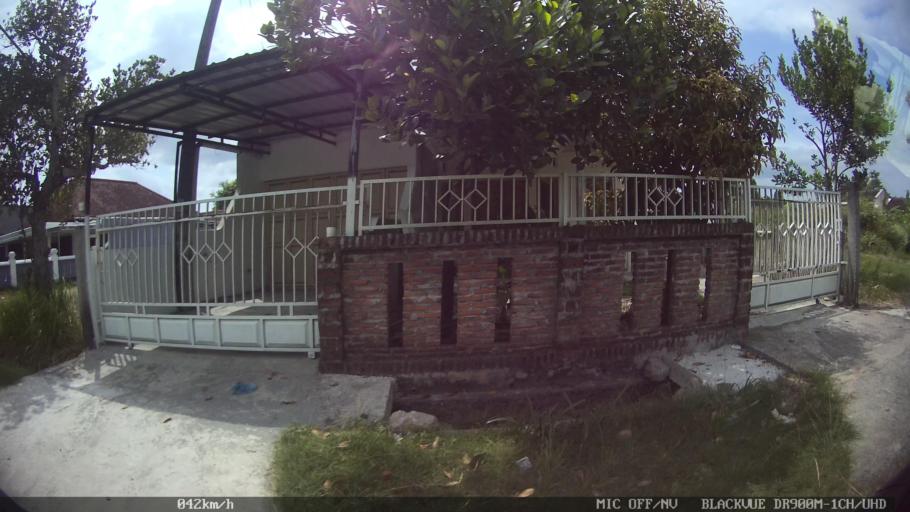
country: ID
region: Daerah Istimewa Yogyakarta
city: Depok
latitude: -7.8144
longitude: 110.4431
